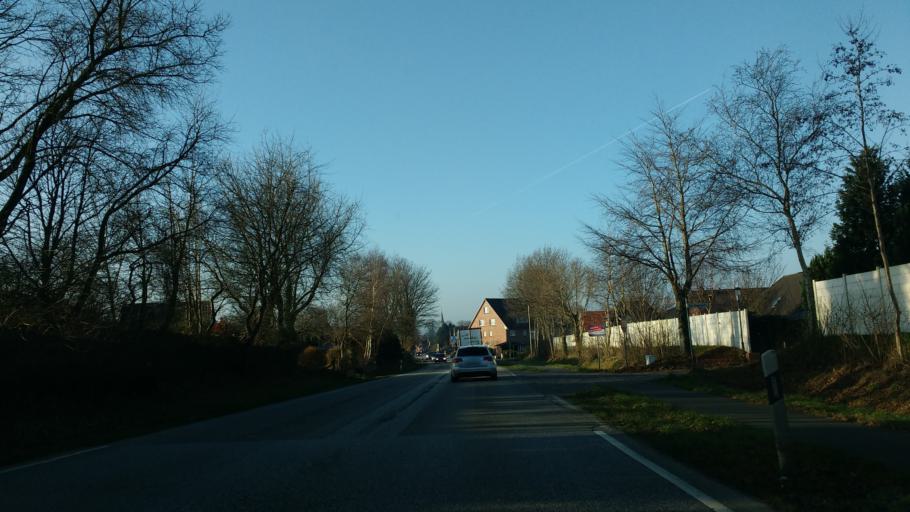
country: DE
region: Schleswig-Holstein
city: Schenefeld
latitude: 54.0472
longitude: 9.4918
